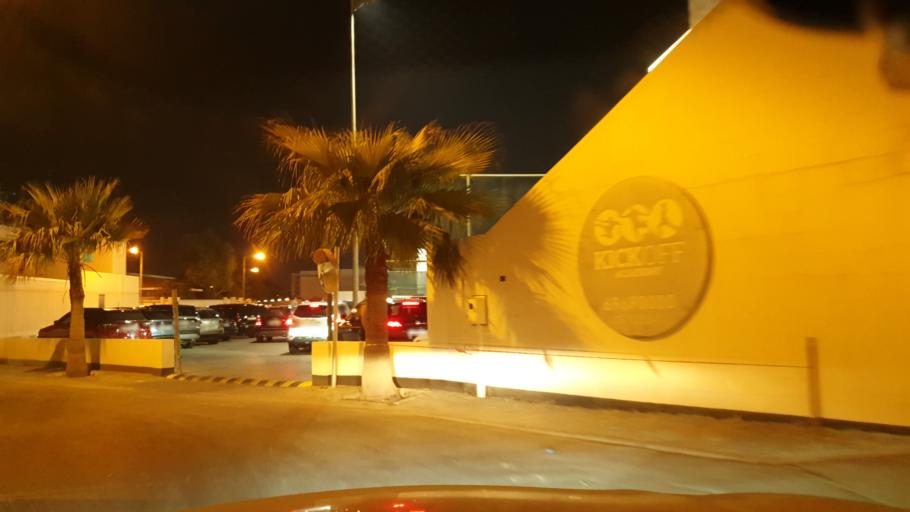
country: BH
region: Northern
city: Madinat `Isa
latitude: 26.1961
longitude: 50.4910
